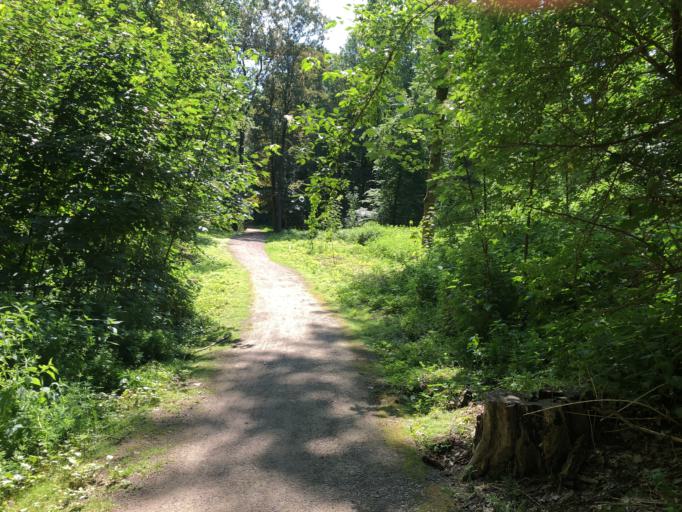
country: DE
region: North Rhine-Westphalia
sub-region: Regierungsbezirk Dusseldorf
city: Erkrath
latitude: 51.1921
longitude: 6.8471
